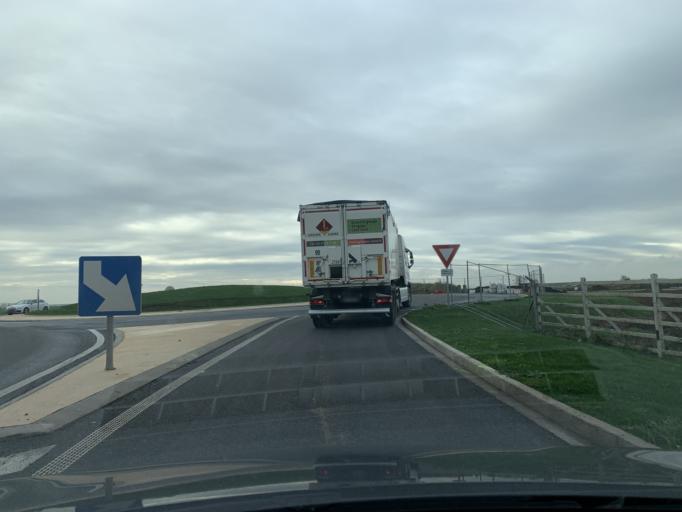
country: FR
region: Nord-Pas-de-Calais
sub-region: Departement du Nord
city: Raillencourt-Sainte-Olle
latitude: 50.2209
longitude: 3.1780
